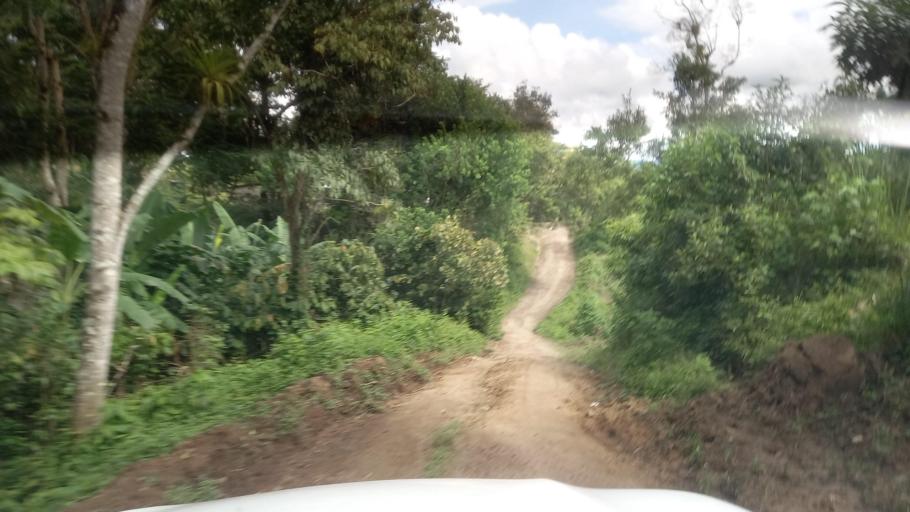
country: NI
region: Jinotega
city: San Jose de Bocay
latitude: 13.4127
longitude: -85.7029
